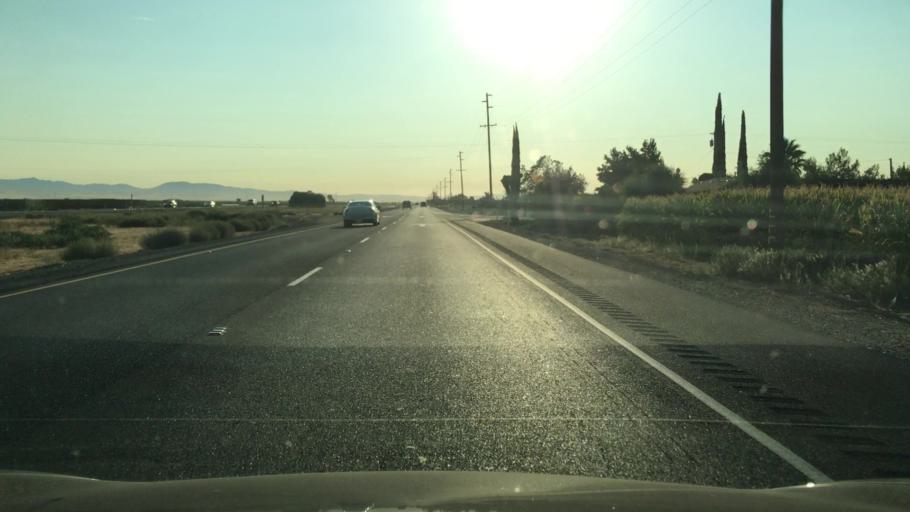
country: US
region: California
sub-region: Merced County
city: South Dos Palos
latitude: 37.0548
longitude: -120.7158
